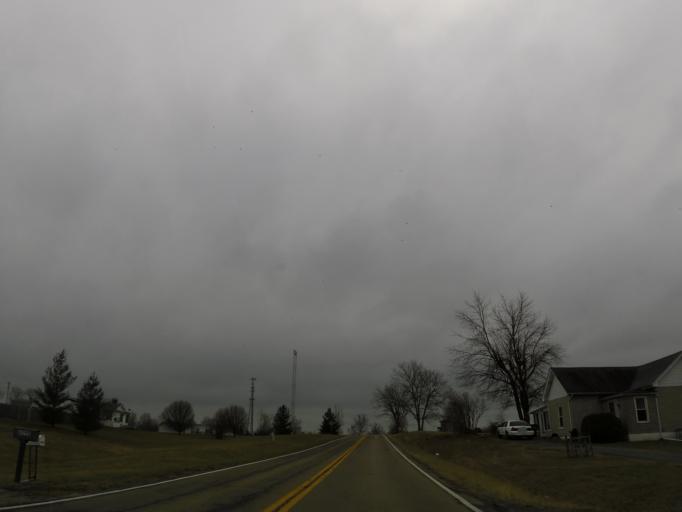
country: US
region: Kentucky
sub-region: Trimble County
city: Providence
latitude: 38.5317
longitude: -85.2558
